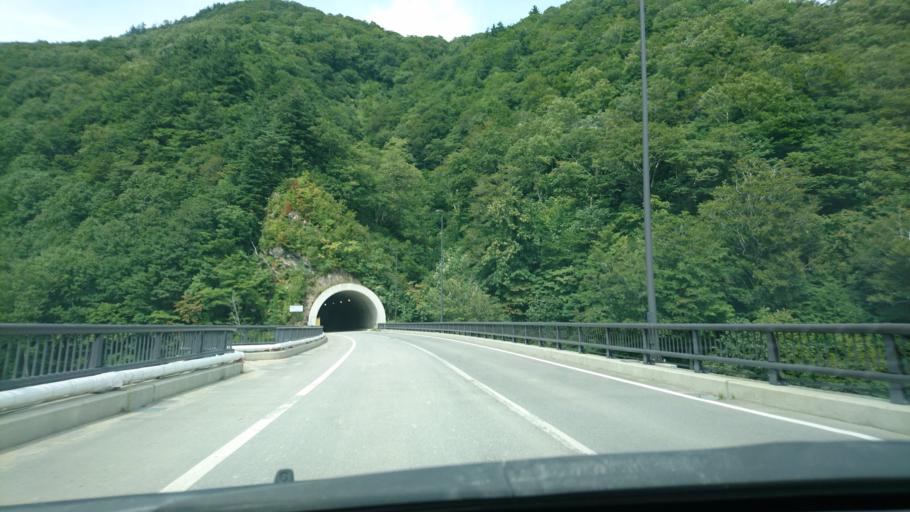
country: JP
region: Akita
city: Yuzawa
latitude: 39.0386
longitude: 140.7349
